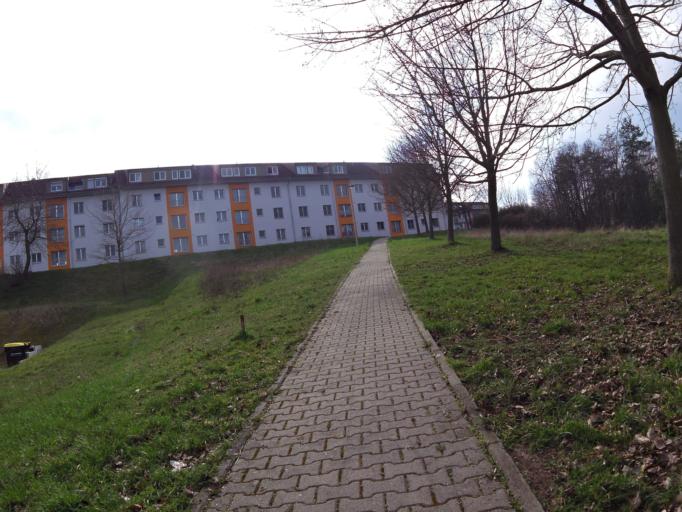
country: DE
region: Bavaria
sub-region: Regierungsbezirk Unterfranken
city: Kitzingen
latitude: 49.7403
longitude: 10.1351
